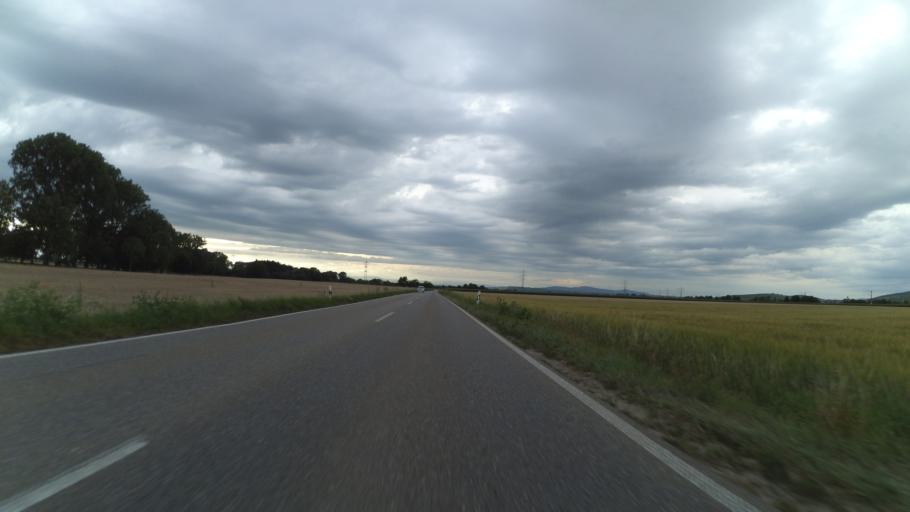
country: DE
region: Baden-Wuerttemberg
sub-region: Freiburg Region
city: Bad Krozingen
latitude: 47.8957
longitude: 7.7243
